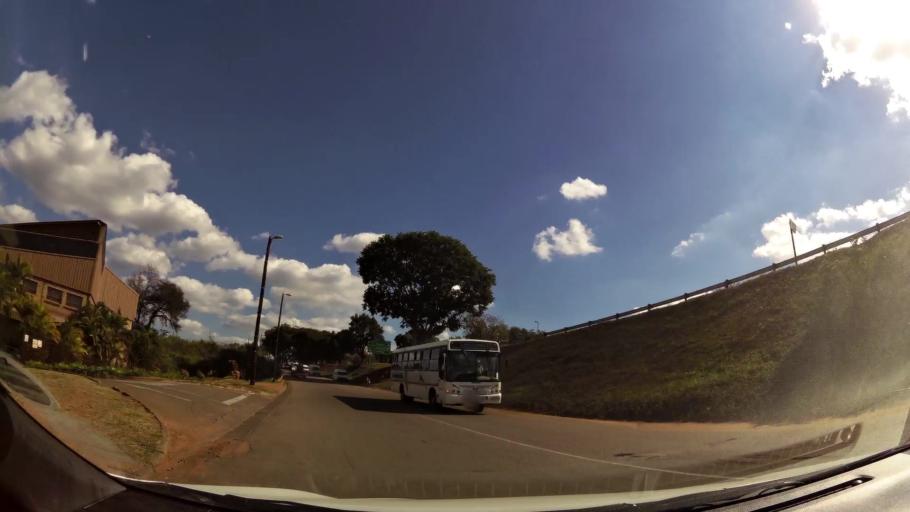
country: ZA
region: Limpopo
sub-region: Mopani District Municipality
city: Tzaneen
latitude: -23.8212
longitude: 30.1627
